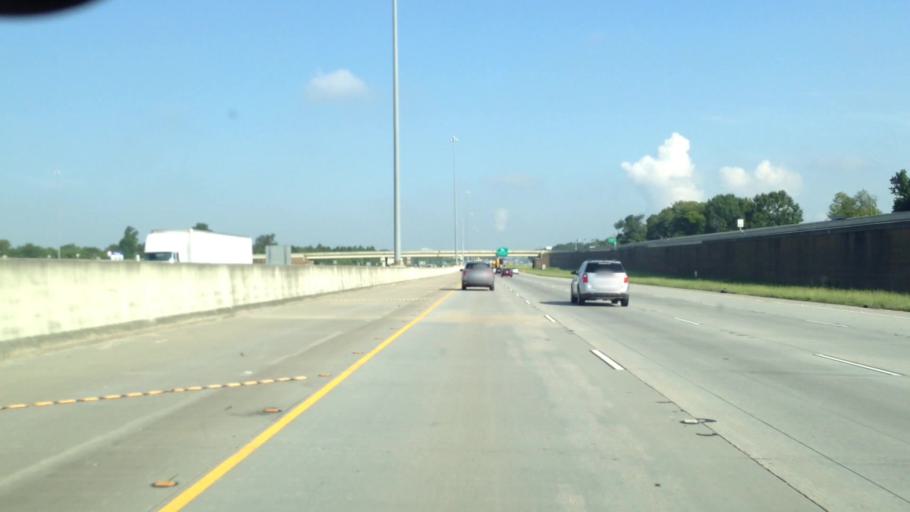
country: US
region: Louisiana
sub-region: East Baton Rouge Parish
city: Inniswold
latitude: 30.3881
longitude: -91.0749
